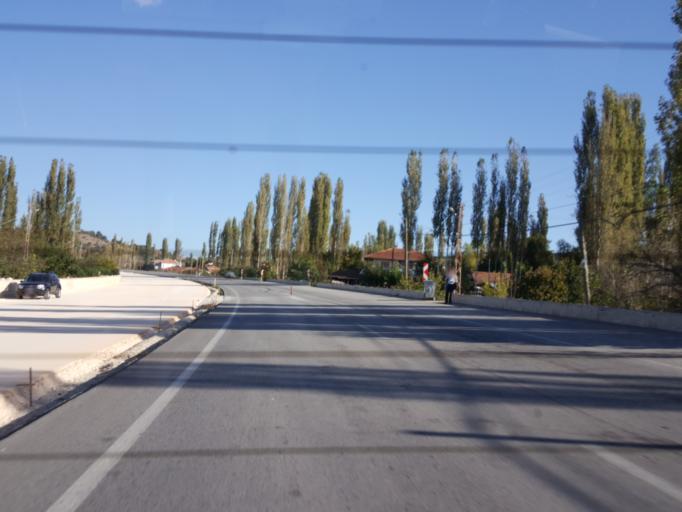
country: TR
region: Amasya
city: Ezinepazari
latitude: 40.5452
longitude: 36.1520
